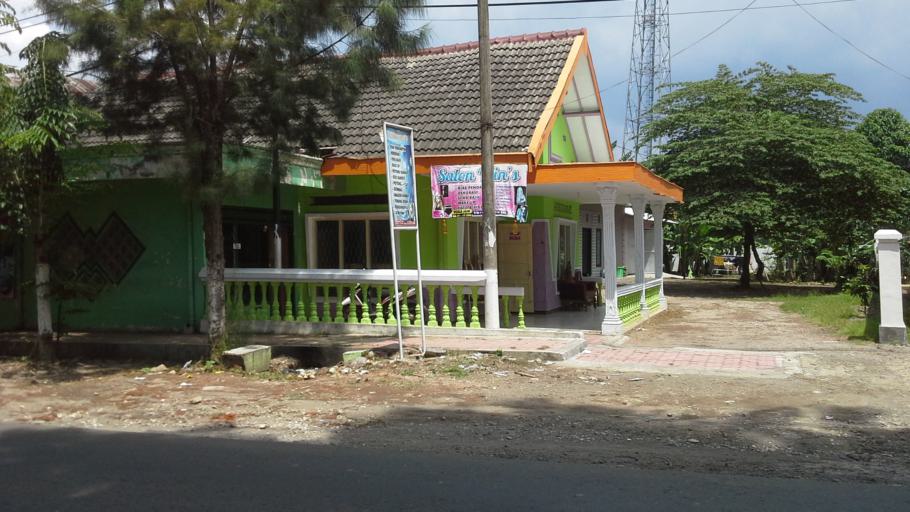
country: ID
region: East Java
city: Maesan
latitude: -8.0289
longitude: 113.7767
